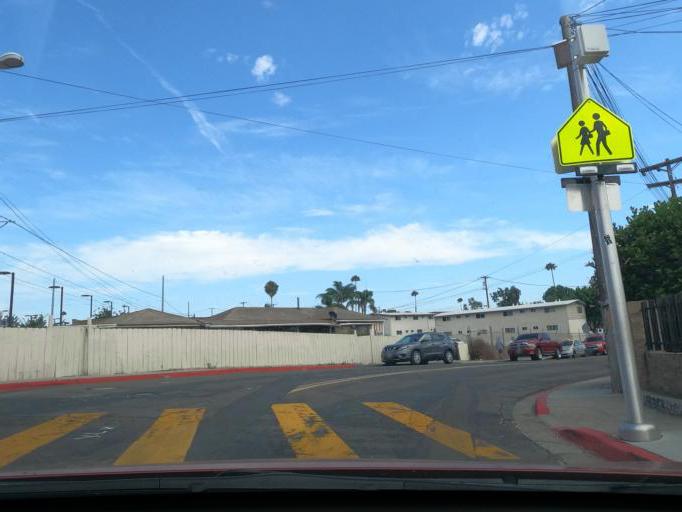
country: US
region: California
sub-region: San Diego County
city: Imperial Beach
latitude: 32.5579
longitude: -117.0481
